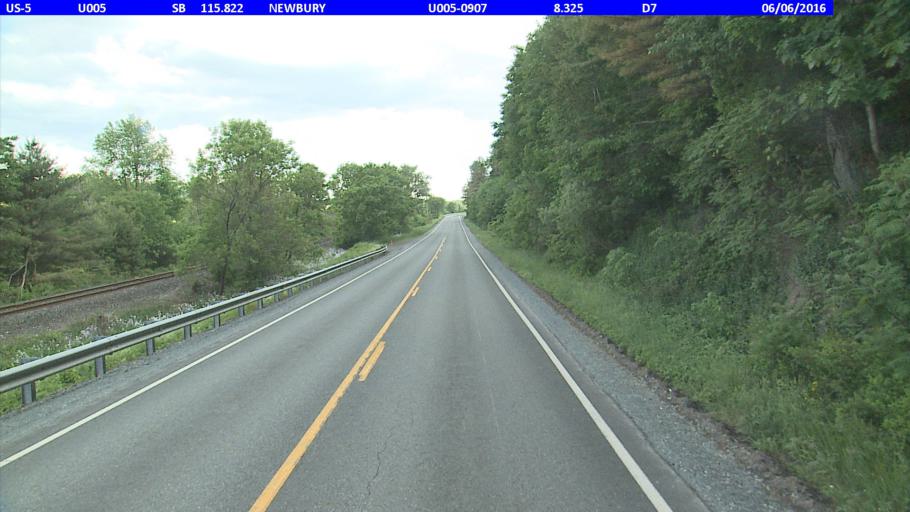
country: US
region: New Hampshire
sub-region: Grafton County
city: Woodsville
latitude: 44.1378
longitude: -72.0424
